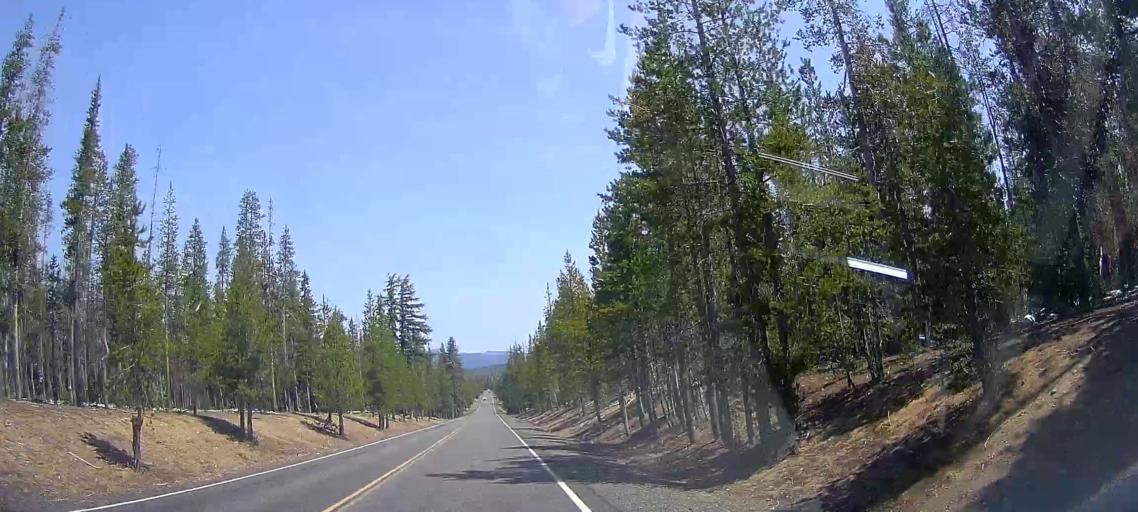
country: US
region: Oregon
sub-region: Jackson County
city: Shady Cove
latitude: 43.0160
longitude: -122.1266
